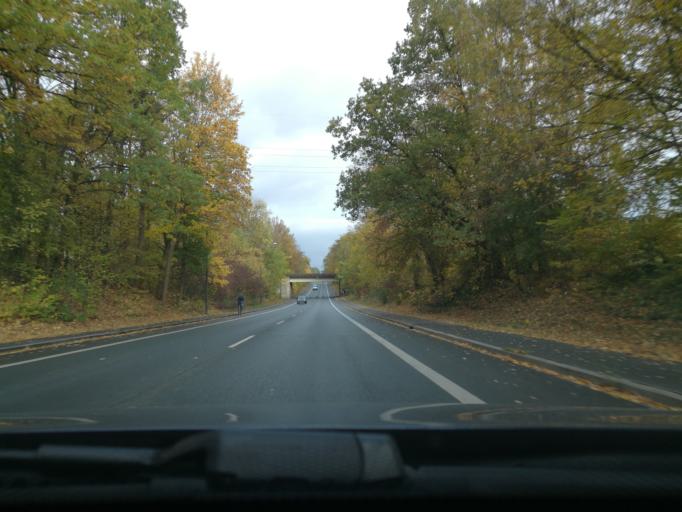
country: DE
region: Bavaria
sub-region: Regierungsbezirk Mittelfranken
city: Furth
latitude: 49.5006
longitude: 10.9828
